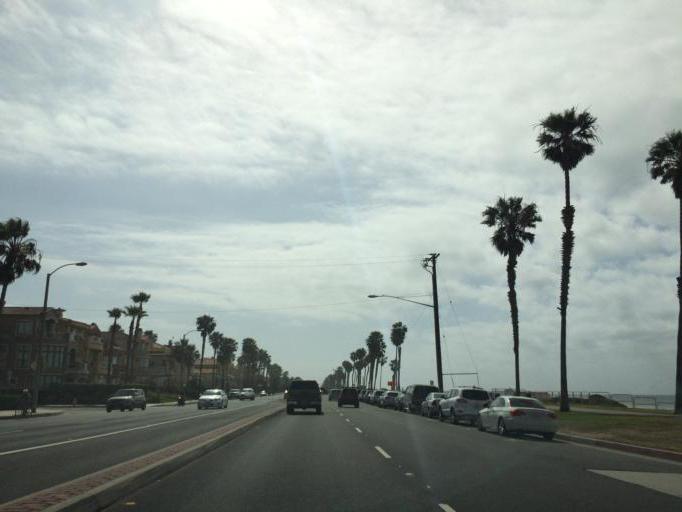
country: US
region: California
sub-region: Orange County
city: Huntington Beach
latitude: 33.6680
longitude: -118.0172
